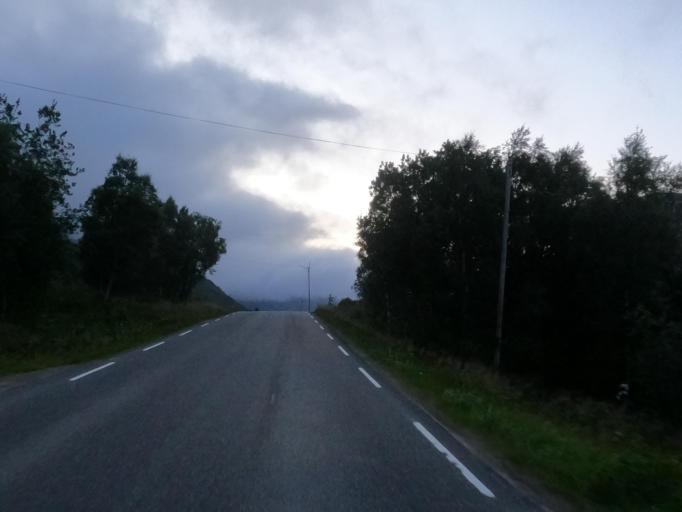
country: NO
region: Nordland
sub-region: Lodingen
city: Lodingen
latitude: 68.5787
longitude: 15.7930
